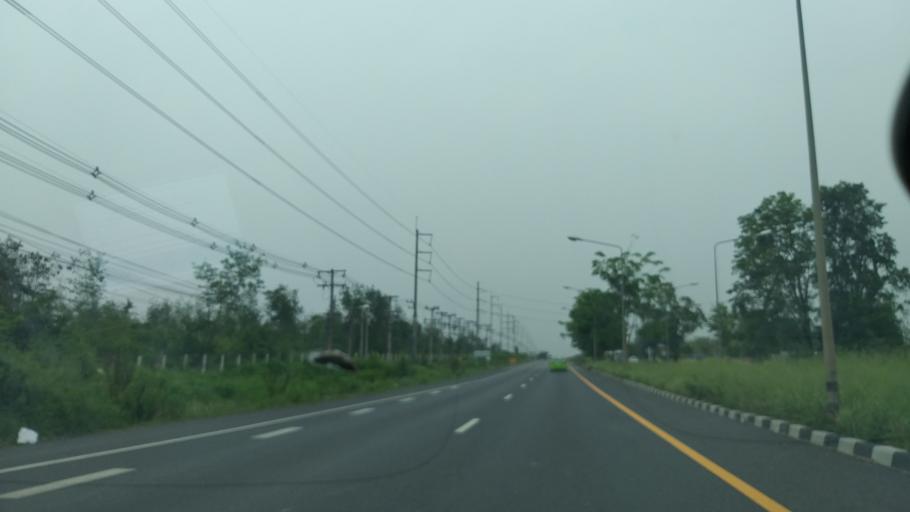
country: TH
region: Chon Buri
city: Ko Chan
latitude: 13.4176
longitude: 101.2823
